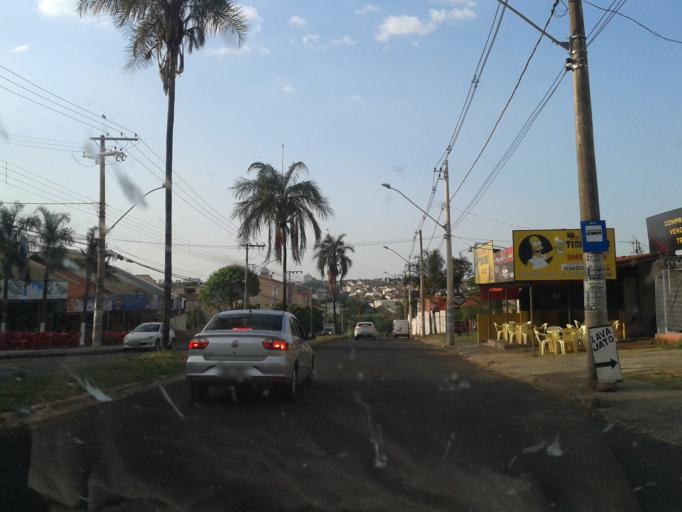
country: BR
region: Minas Gerais
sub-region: Uberlandia
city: Uberlandia
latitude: -18.9245
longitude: -48.3221
